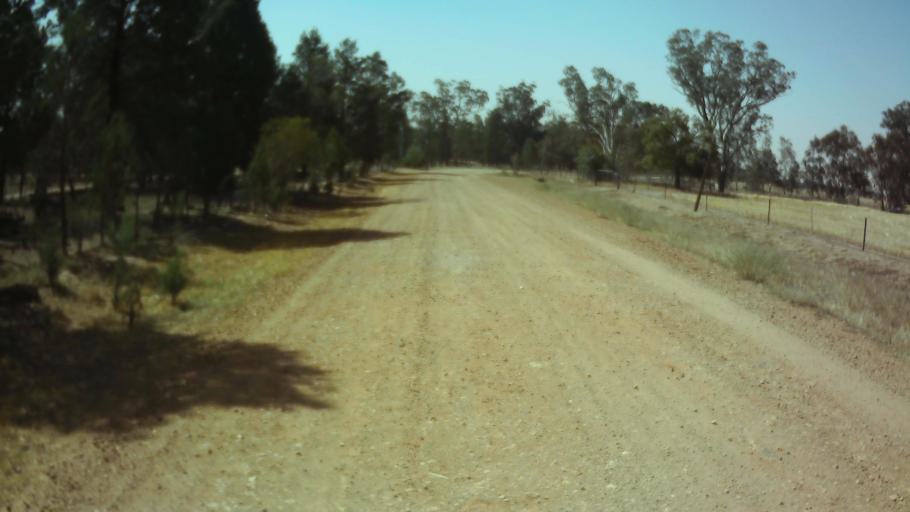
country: AU
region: New South Wales
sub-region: Weddin
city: Grenfell
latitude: -33.9487
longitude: 147.9286
